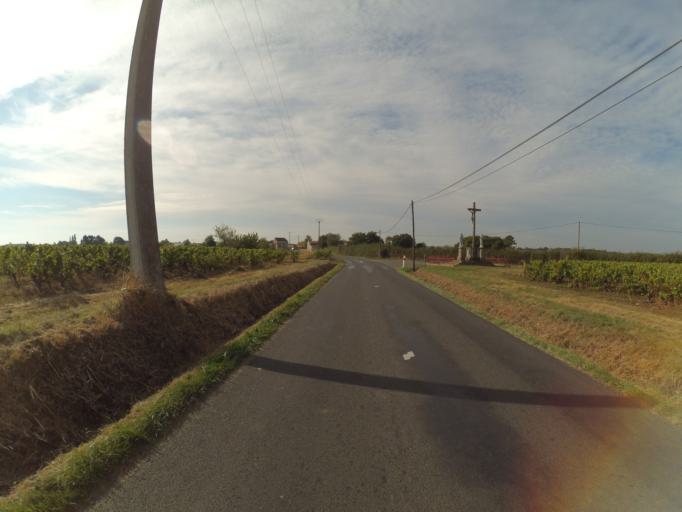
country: FR
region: Pays de la Loire
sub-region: Departement de Maine-et-Loire
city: Tillieres
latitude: 47.1498
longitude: -1.1653
